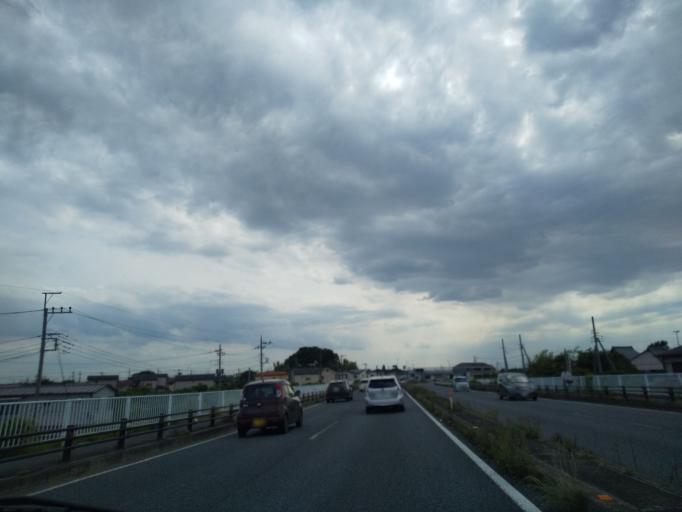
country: JP
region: Chiba
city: Noda
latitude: 35.9896
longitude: 139.8156
